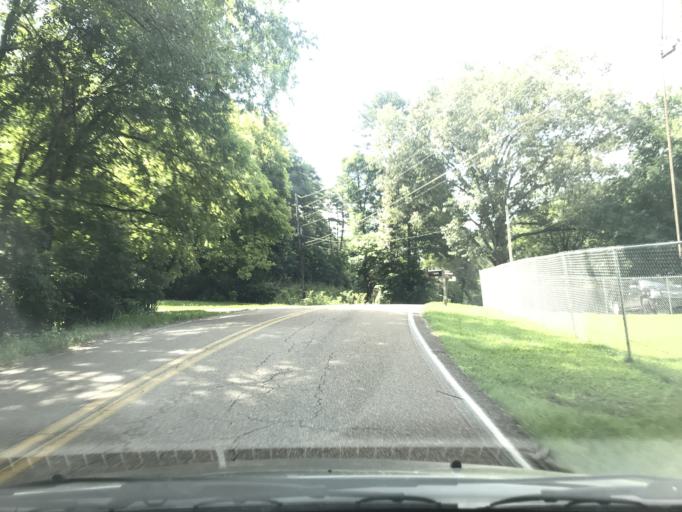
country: US
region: Tennessee
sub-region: Hamilton County
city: Lakesite
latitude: 35.1791
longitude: -85.0656
